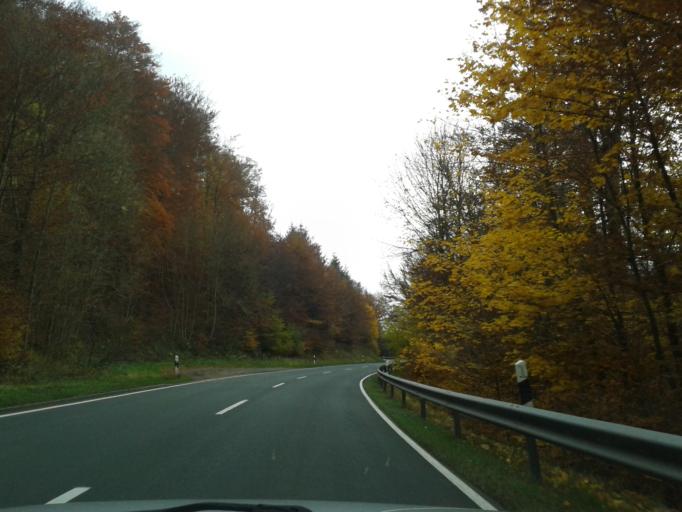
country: DE
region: North Rhine-Westphalia
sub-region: Regierungsbezirk Arnsberg
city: Erndtebruck
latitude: 50.9728
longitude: 8.3392
